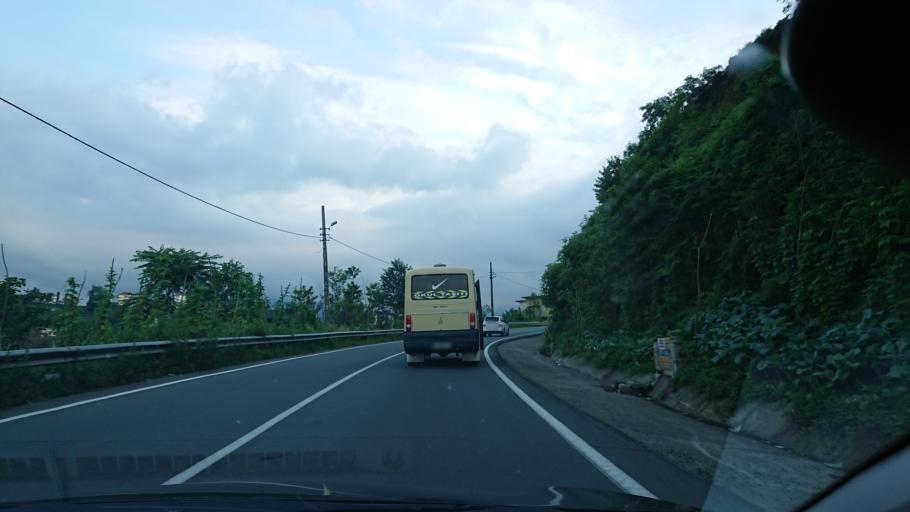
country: TR
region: Rize
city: Cayeli
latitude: 41.0786
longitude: 40.7134
